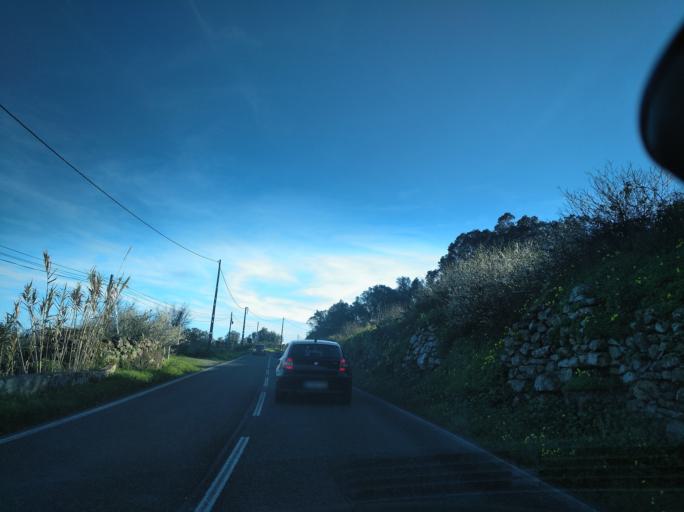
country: PT
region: Lisbon
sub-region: Sintra
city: Pero Pinheiro
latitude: 38.8809
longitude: -9.3300
